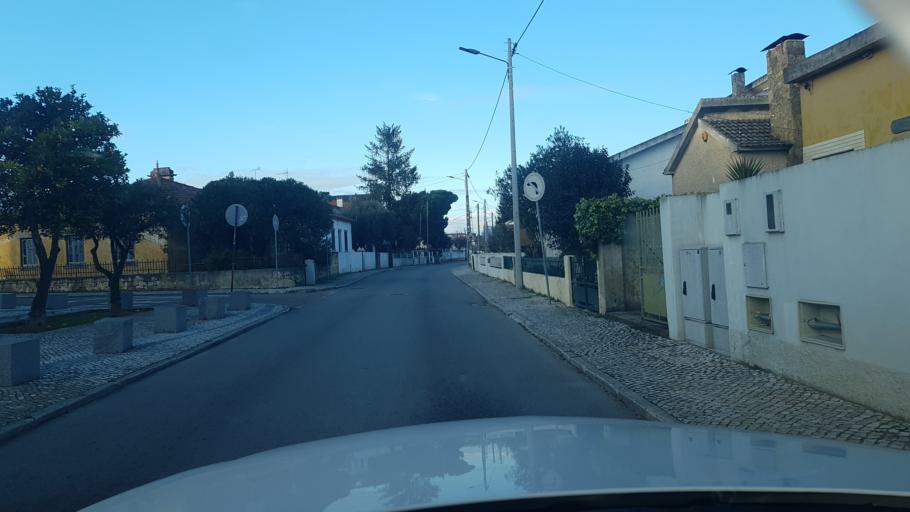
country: PT
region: Santarem
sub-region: Entroncamento
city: Entroncamento
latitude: 39.4666
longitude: -8.4659
